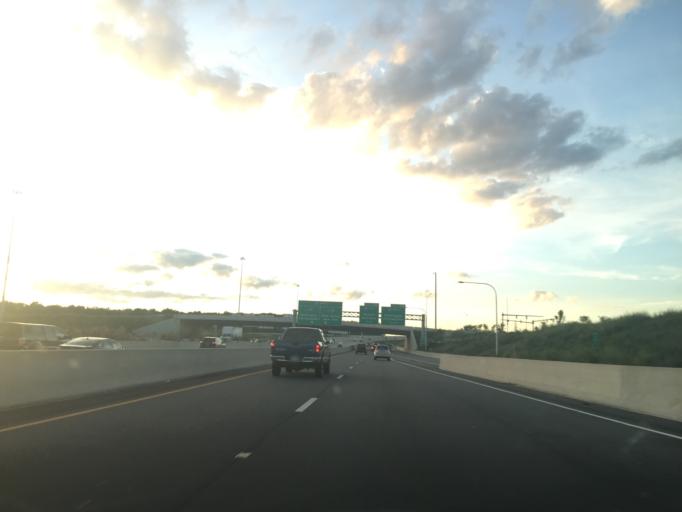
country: US
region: Delaware
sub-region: New Castle County
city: Bear
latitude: 39.6751
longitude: -75.6545
